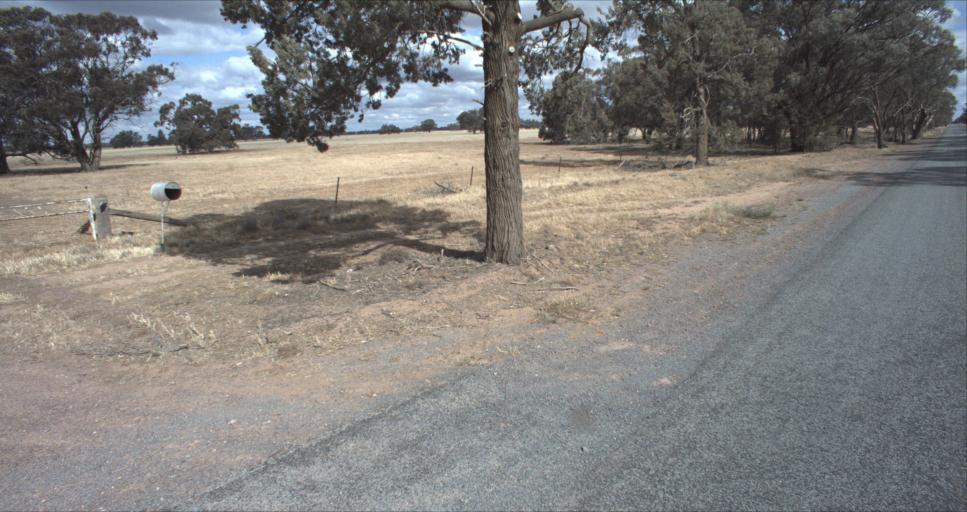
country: AU
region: New South Wales
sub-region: Leeton
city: Leeton
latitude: -34.6623
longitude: 146.3491
